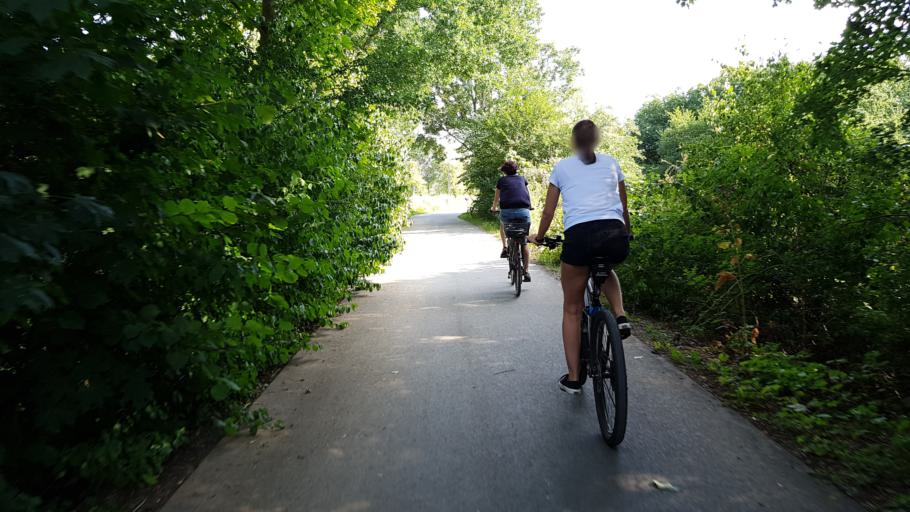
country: DE
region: Hesse
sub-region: Regierungsbezirk Darmstadt
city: Karben
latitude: 50.2362
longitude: 8.7636
